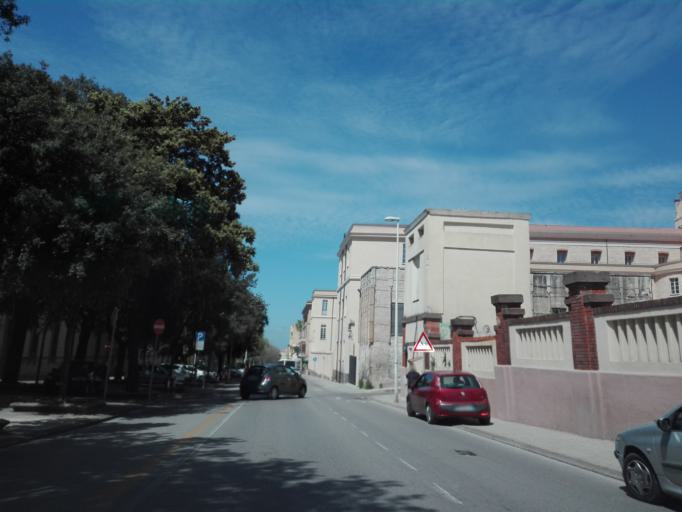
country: IT
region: Sardinia
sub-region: Provincia di Sassari
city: Sassari
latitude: 40.7219
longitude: 8.5633
